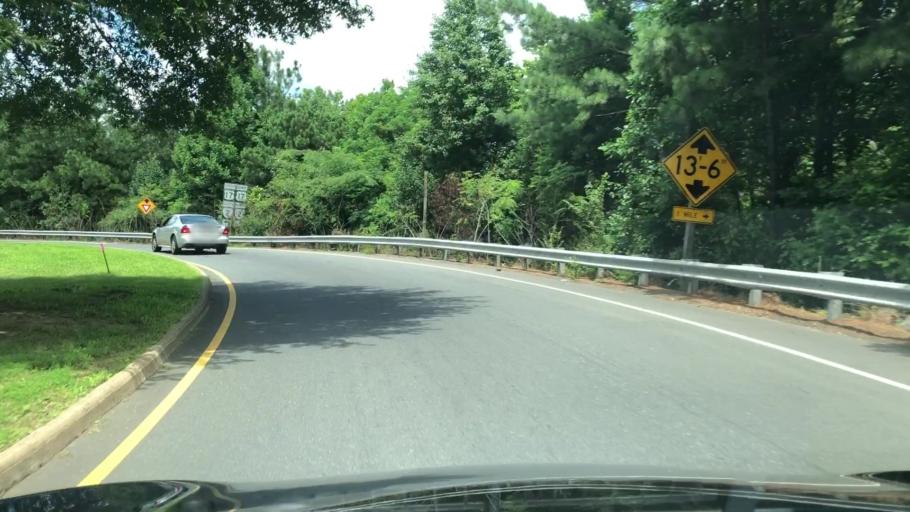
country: US
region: Virginia
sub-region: City of Fredericksburg
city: Fredericksburg
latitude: 38.2914
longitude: -77.4553
